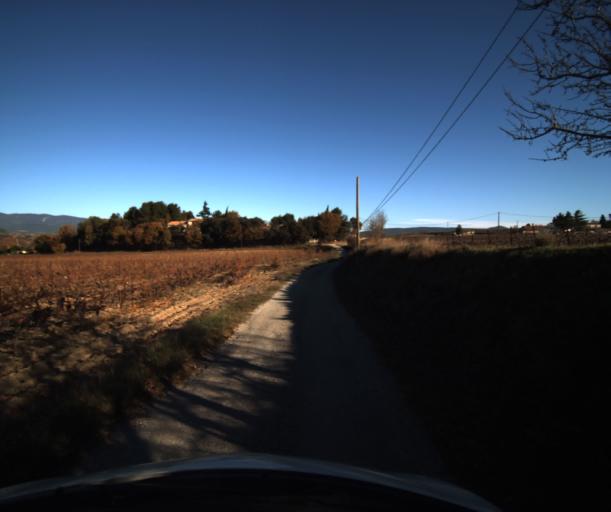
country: FR
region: Provence-Alpes-Cote d'Azur
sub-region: Departement du Vaucluse
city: Pertuis
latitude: 43.7024
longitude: 5.5260
